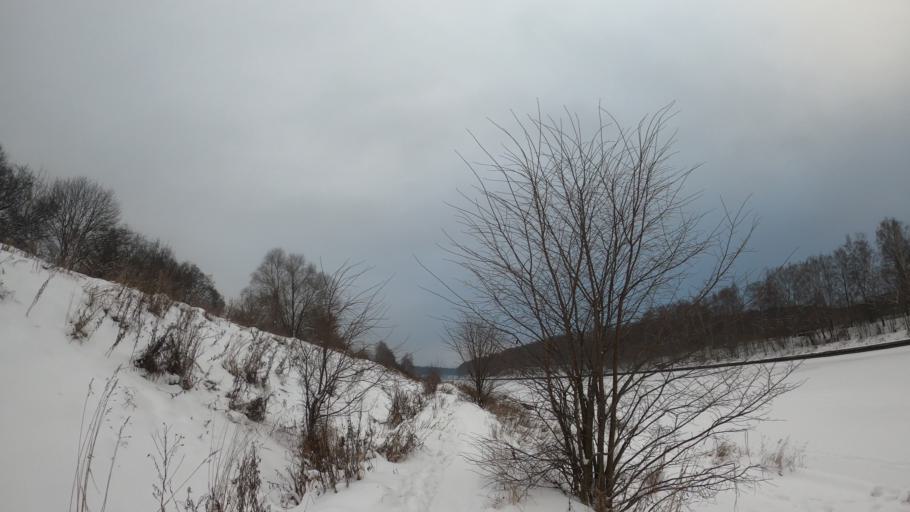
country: RU
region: Moskovskaya
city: Dolgoprudnyy
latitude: 55.9432
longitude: 37.4807
